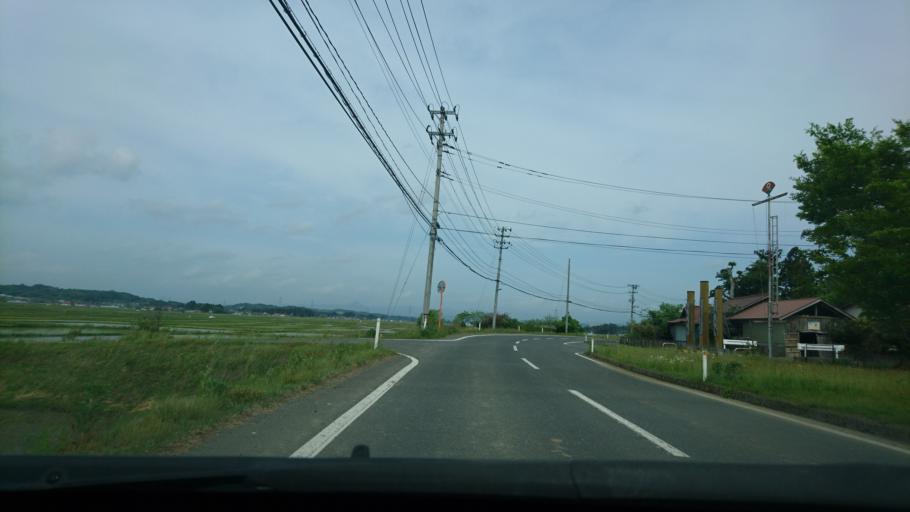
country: JP
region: Iwate
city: Ichinoseki
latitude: 38.8083
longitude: 141.0668
